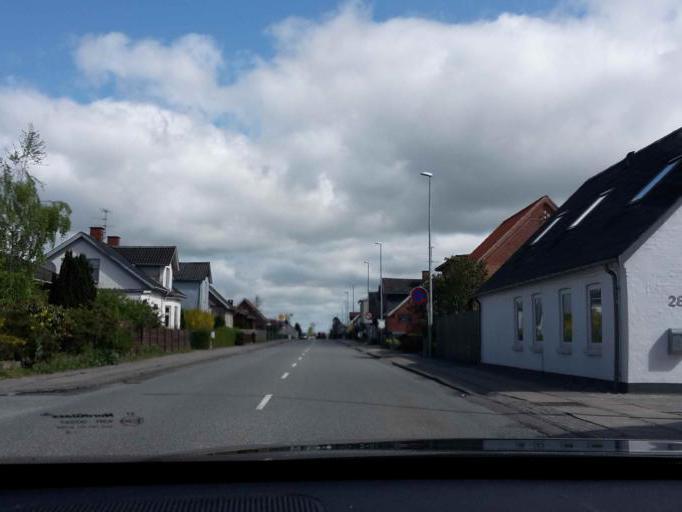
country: DK
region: Central Jutland
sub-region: Syddjurs Kommune
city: Hornslet
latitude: 56.3173
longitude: 10.3219
